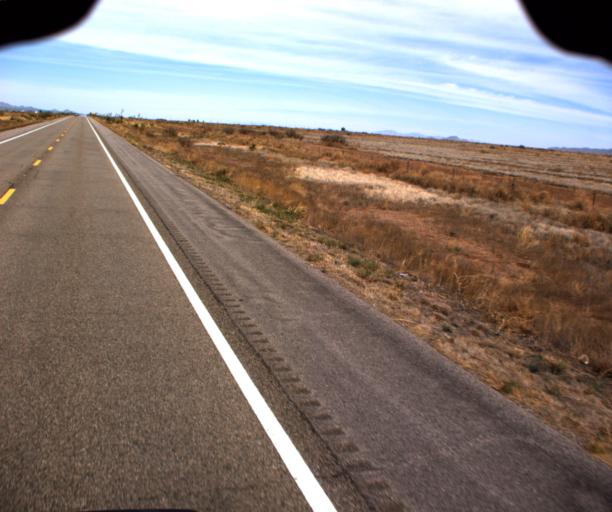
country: US
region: Arizona
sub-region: Cochise County
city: Pirtleville
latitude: 31.5349
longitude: -109.6537
